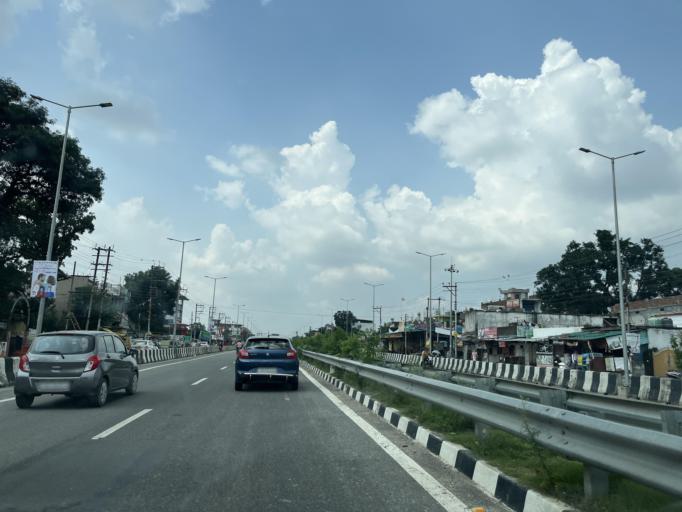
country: IN
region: Uttarakhand
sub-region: Dehradun
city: Raipur
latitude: 30.2567
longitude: 78.0917
